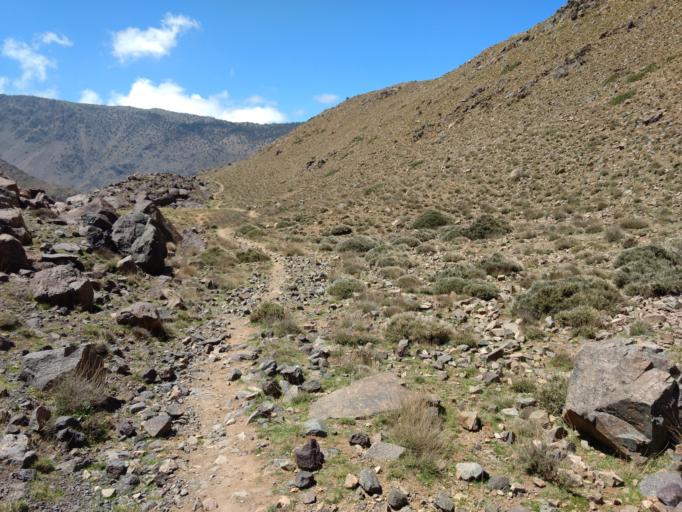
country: MA
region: Marrakech-Tensift-Al Haouz
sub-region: Al-Haouz
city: Moulay Brahim
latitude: 31.1289
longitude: -7.9075
